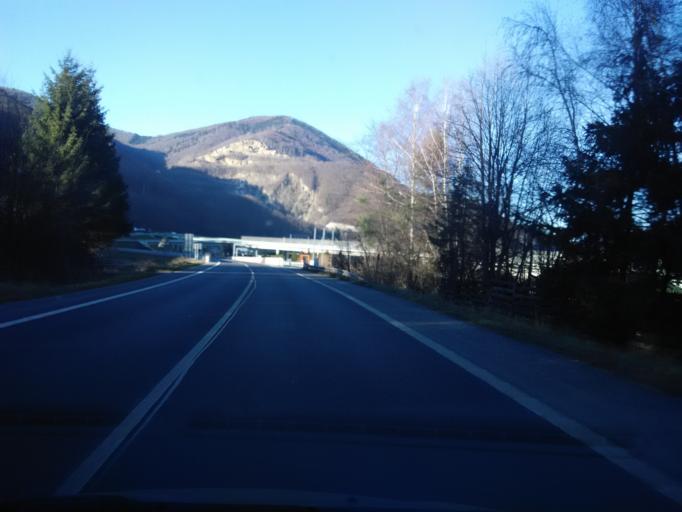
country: SK
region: Zilinsky
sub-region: Okres Zilina
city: Vrutky
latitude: 49.1314
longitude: 18.8990
